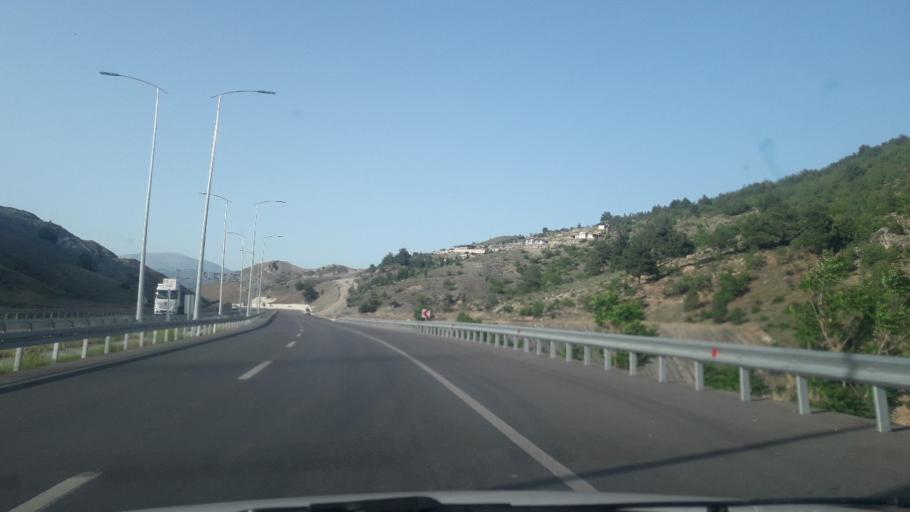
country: TR
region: Amasya
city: Amasya
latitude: 40.6646
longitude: 35.7975
